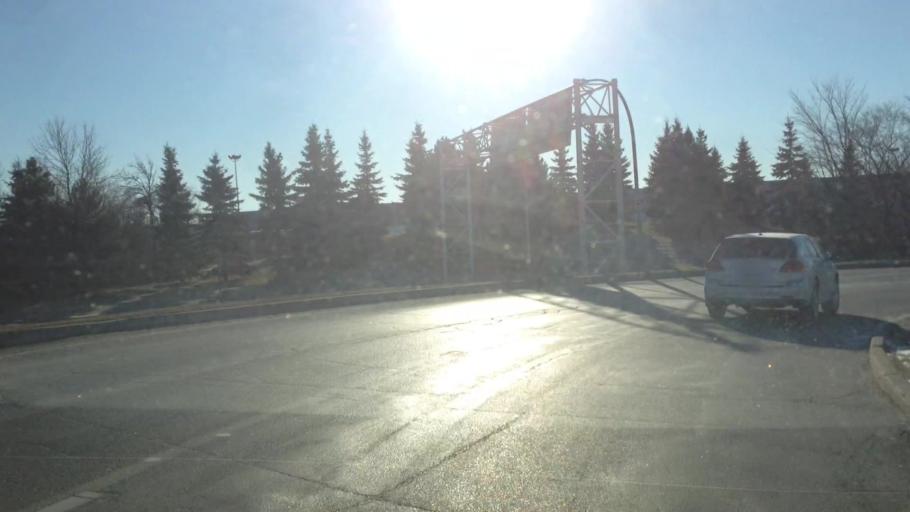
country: CA
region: Quebec
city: Dollard-Des Ormeaux
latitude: 45.4789
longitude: -73.7925
